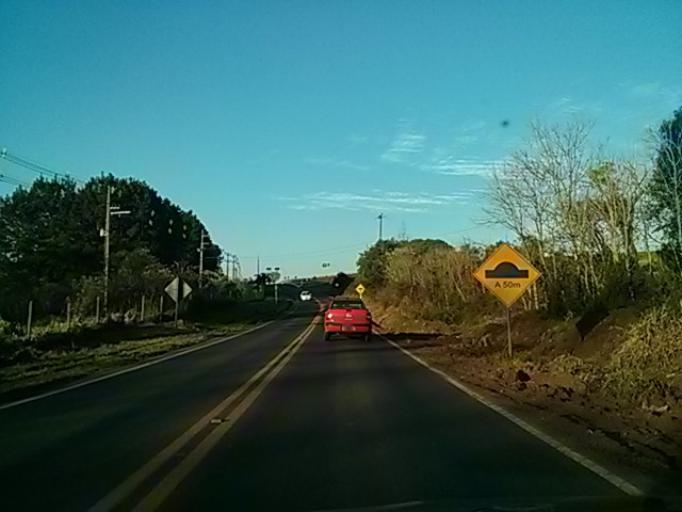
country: BR
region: Santa Catarina
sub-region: Chapeco
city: Chapeco
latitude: -27.1043
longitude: -52.7057
